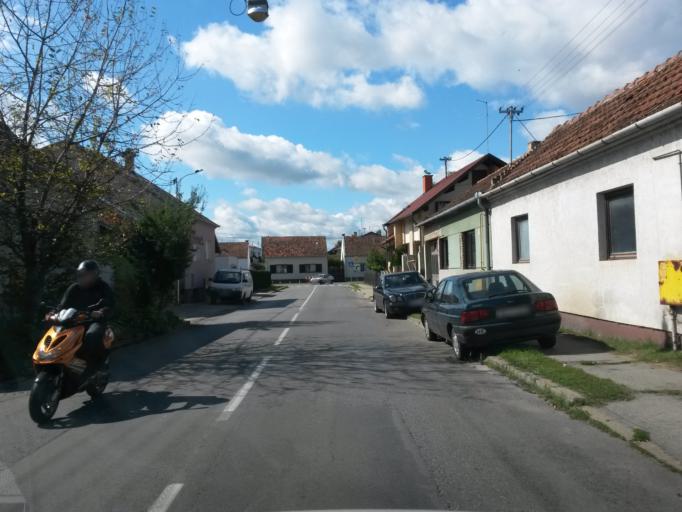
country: HR
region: Osjecko-Baranjska
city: Visnjevac
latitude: 45.5577
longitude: 18.6487
